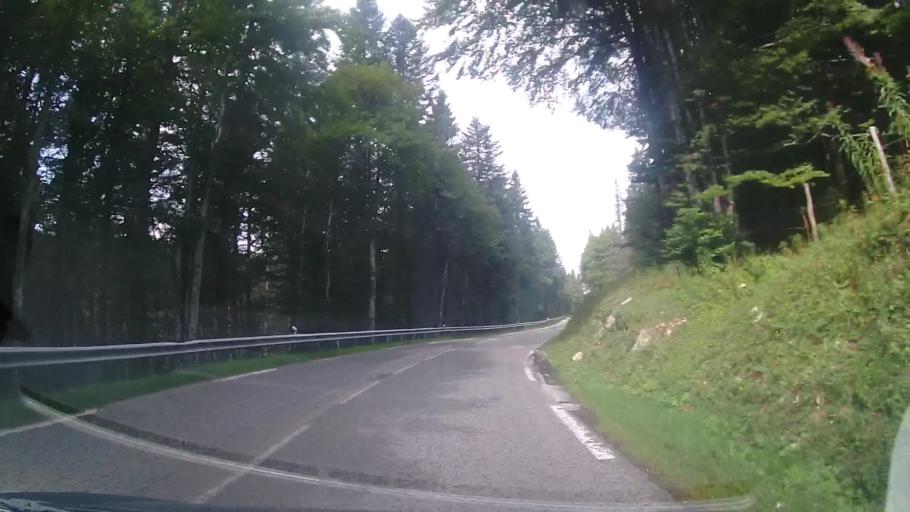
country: FR
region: Franche-Comte
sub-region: Departement du Jura
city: Les Rousses
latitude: 46.4194
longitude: 6.0649
